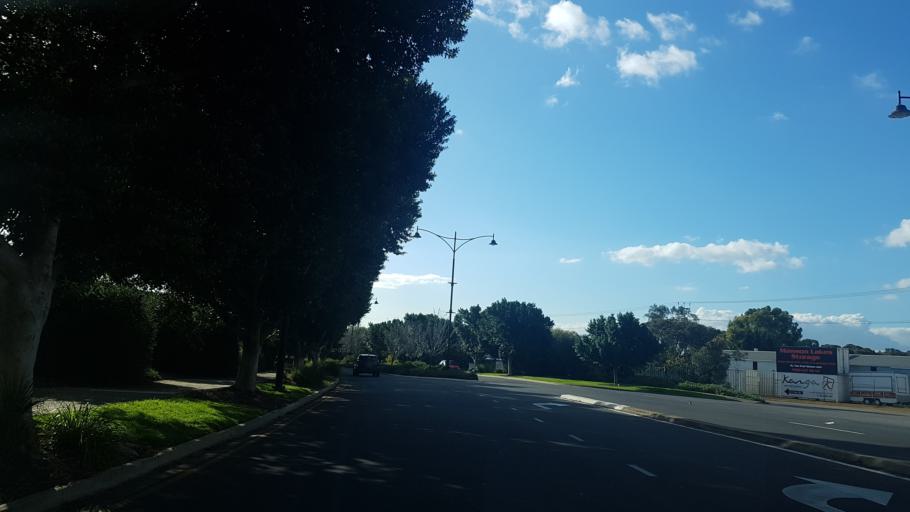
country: AU
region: South Australia
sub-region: Salisbury
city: Ingle Farm
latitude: -34.8244
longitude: 138.6140
